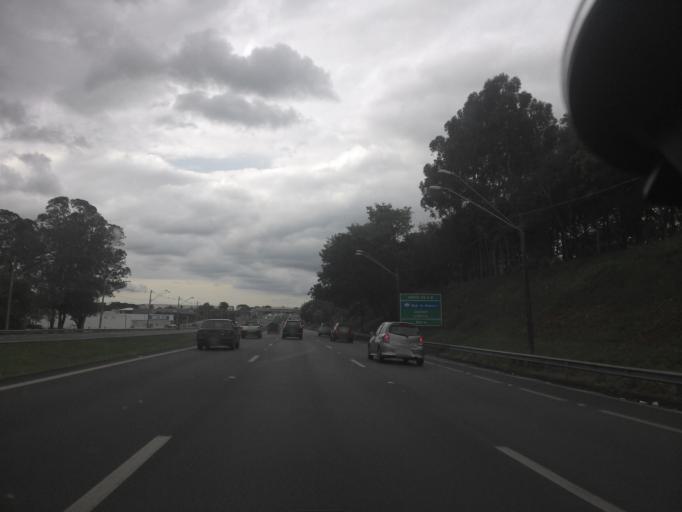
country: BR
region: Sao Paulo
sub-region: Campinas
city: Campinas
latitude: -22.8543
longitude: -47.0745
